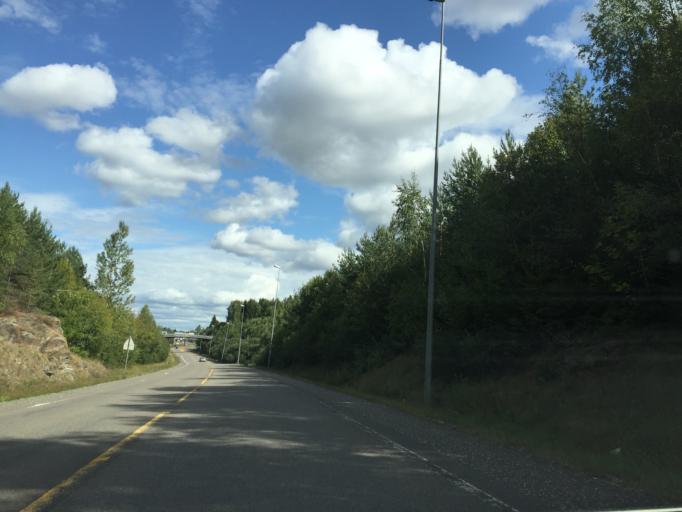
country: NO
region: Ostfold
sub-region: Hobol
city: Knappstad
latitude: 59.6165
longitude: 11.0462
